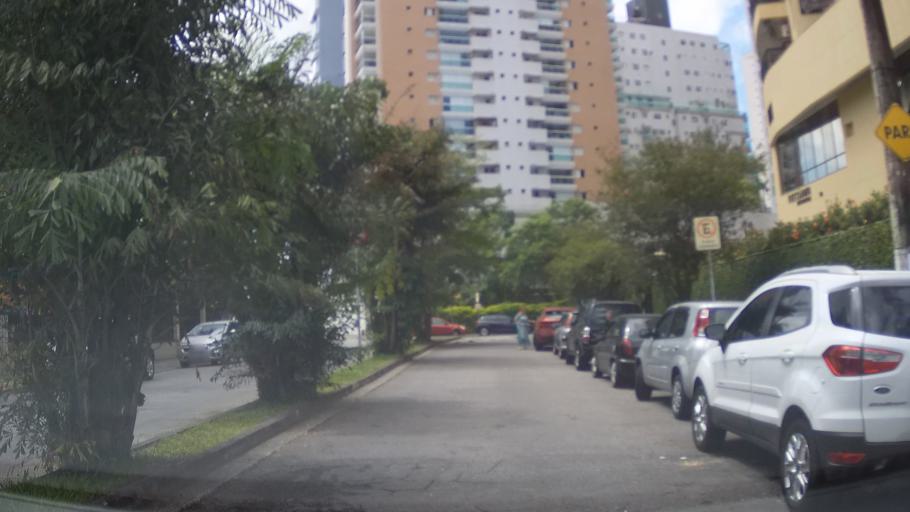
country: BR
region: Sao Paulo
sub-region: Guaruja
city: Guaruja
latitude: -23.9866
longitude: -46.2988
